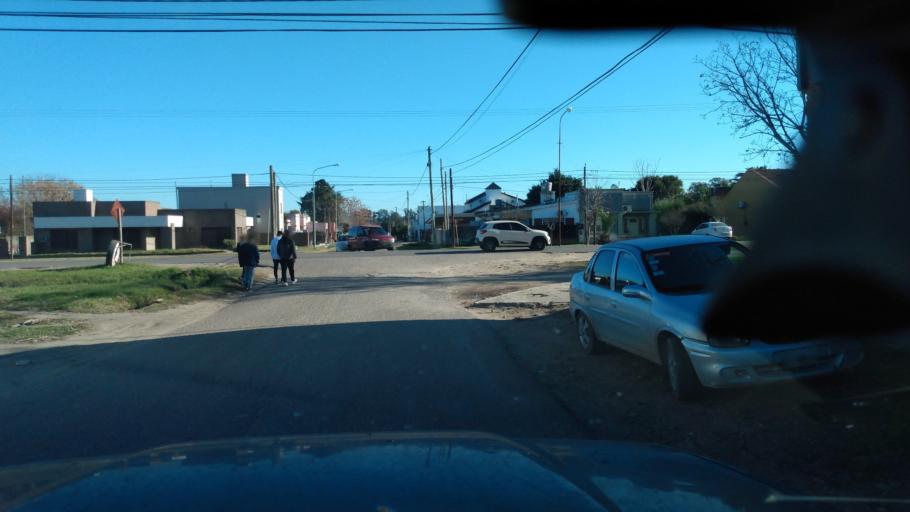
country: AR
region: Buenos Aires
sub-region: Partido de Lujan
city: Lujan
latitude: -34.5698
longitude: -59.1819
